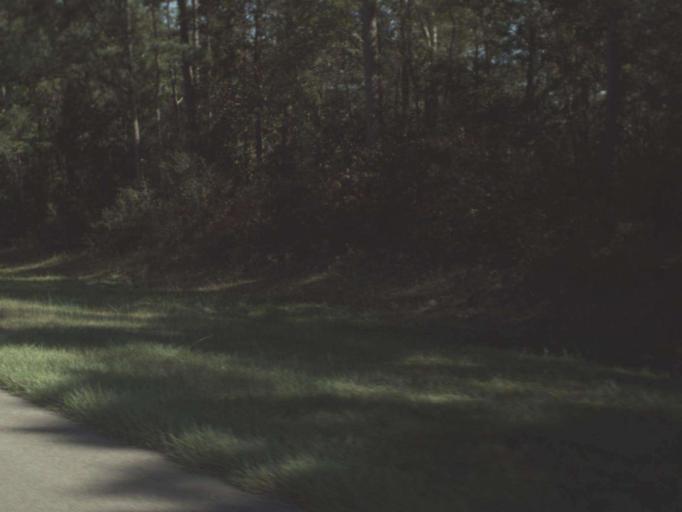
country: US
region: Alabama
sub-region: Covington County
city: Florala
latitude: 30.9669
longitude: -86.3817
